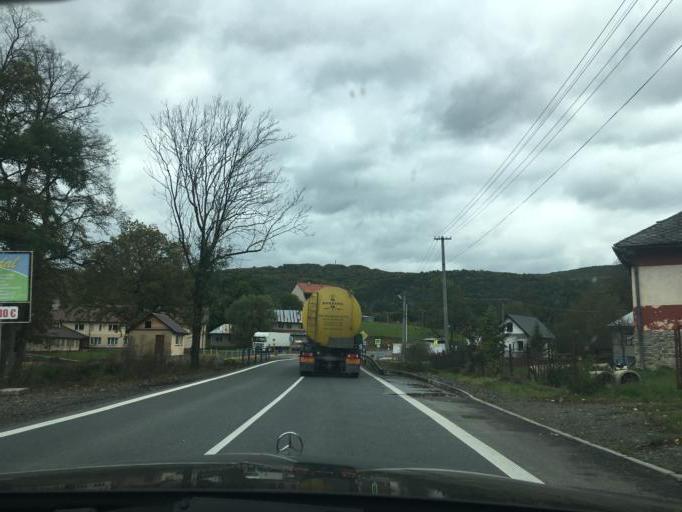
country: SK
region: Presovsky
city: Stropkov
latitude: 49.2134
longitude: 21.5641
